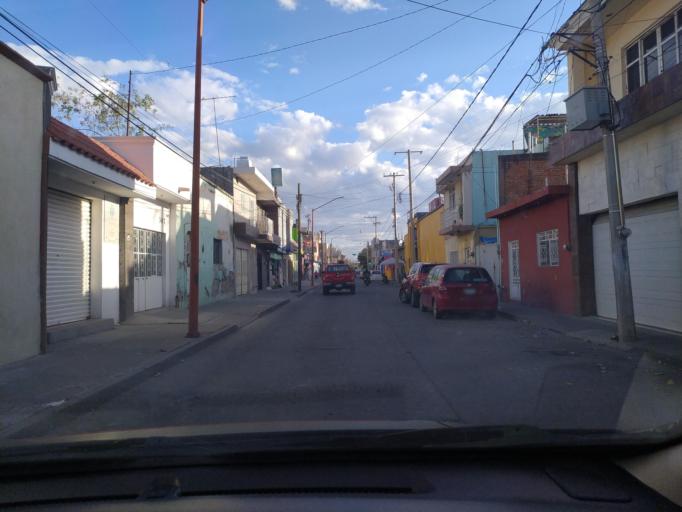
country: LA
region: Oudomxai
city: Muang La
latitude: 21.0173
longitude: 101.8535
